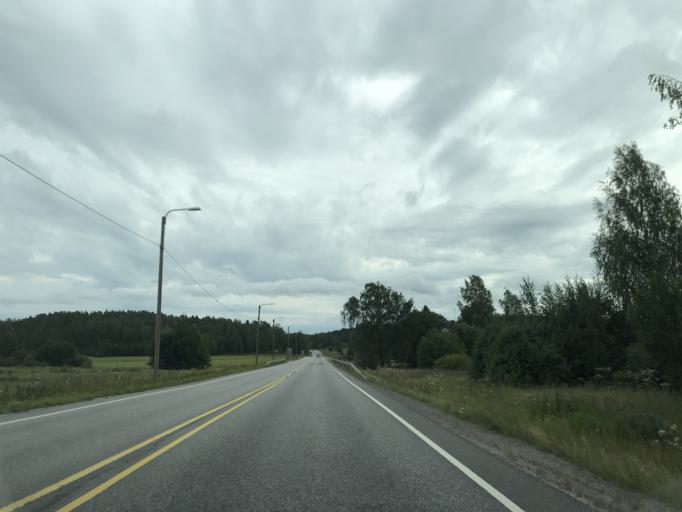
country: FI
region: Varsinais-Suomi
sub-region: Turku
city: Piikkioe
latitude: 60.4343
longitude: 22.5898
